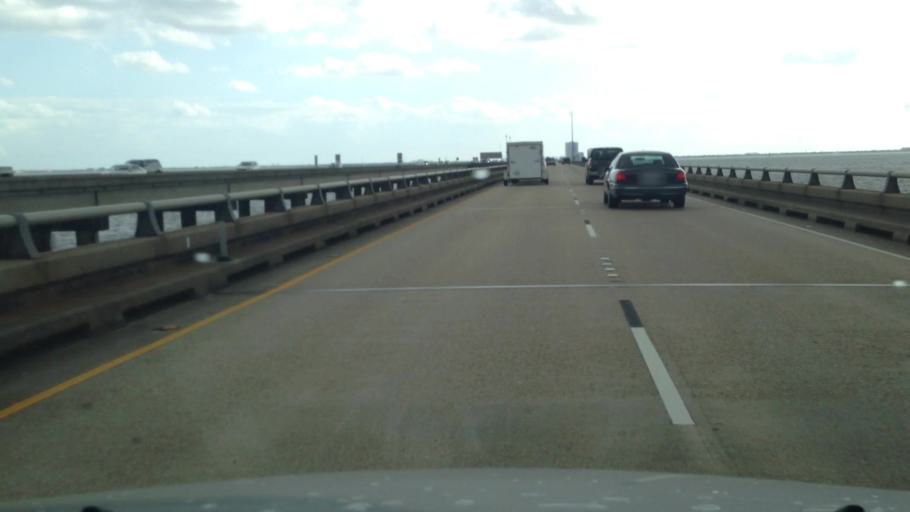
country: US
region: Louisiana
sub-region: Jefferson Parish
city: Metairie
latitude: 30.0735
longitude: -90.1450
